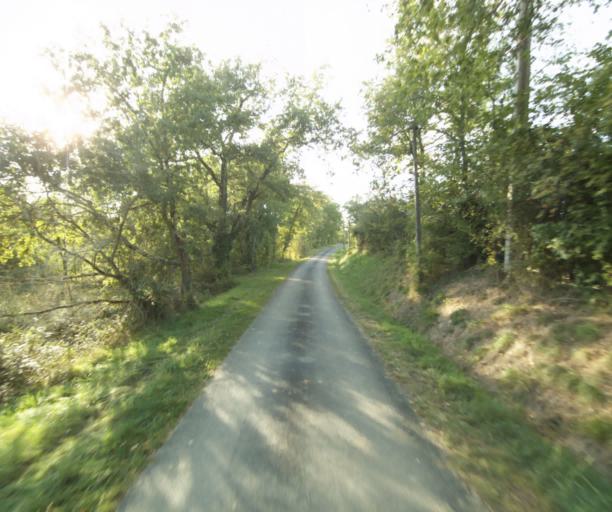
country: FR
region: Midi-Pyrenees
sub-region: Departement du Gers
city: Gondrin
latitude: 43.8883
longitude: 0.2494
